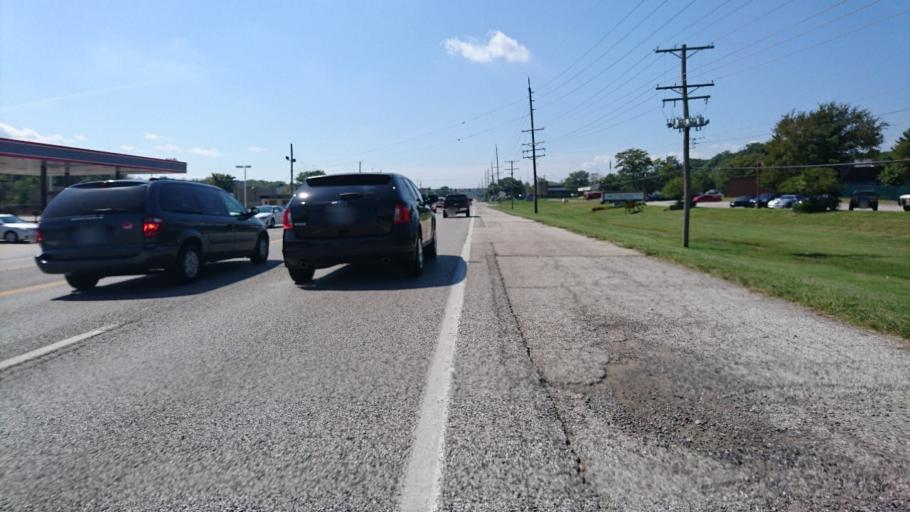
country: US
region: Missouri
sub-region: Saint Louis County
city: Manchester
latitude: 38.5964
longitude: -90.4881
